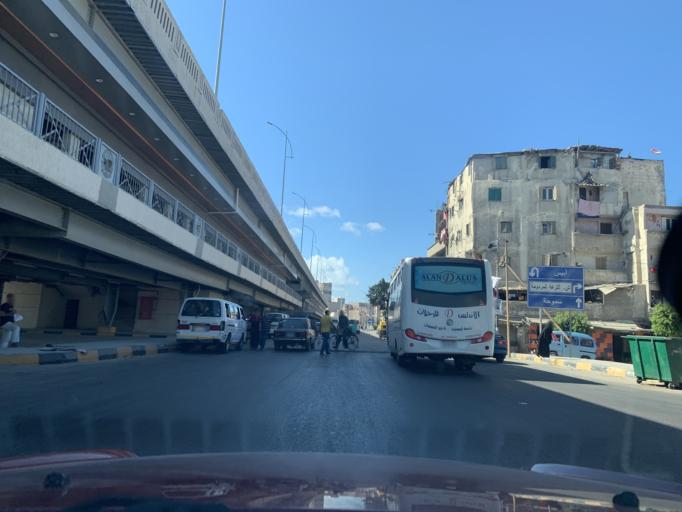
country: EG
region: Alexandria
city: Alexandria
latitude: 31.2240
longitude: 29.9836
